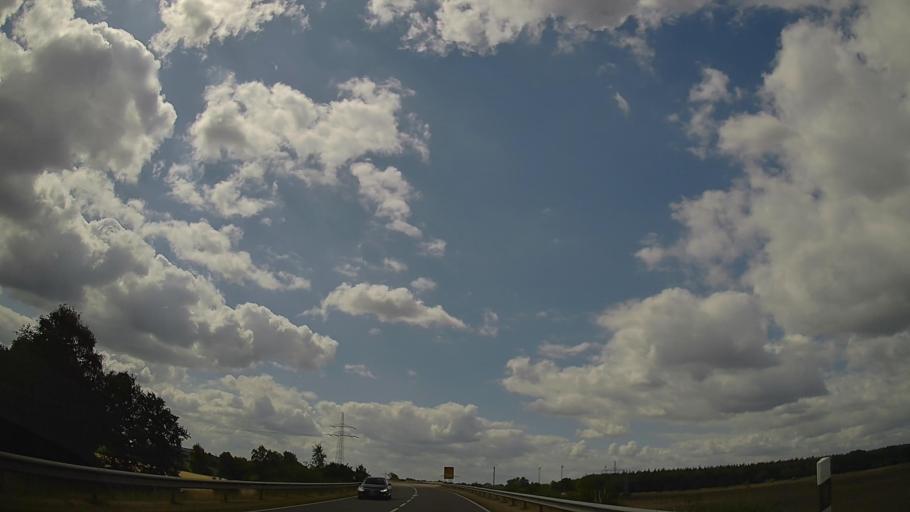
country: DE
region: Lower Saxony
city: Vechta
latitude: 52.7332
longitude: 8.2521
